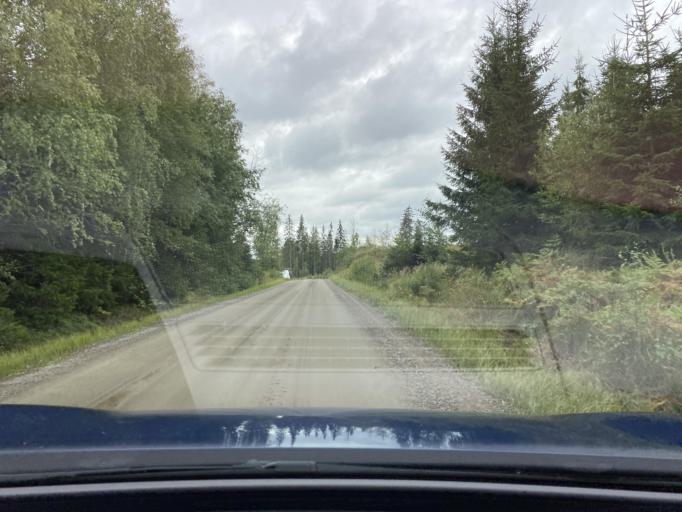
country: FI
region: Pirkanmaa
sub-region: Lounais-Pirkanmaa
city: Punkalaidun
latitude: 61.1895
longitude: 23.1836
